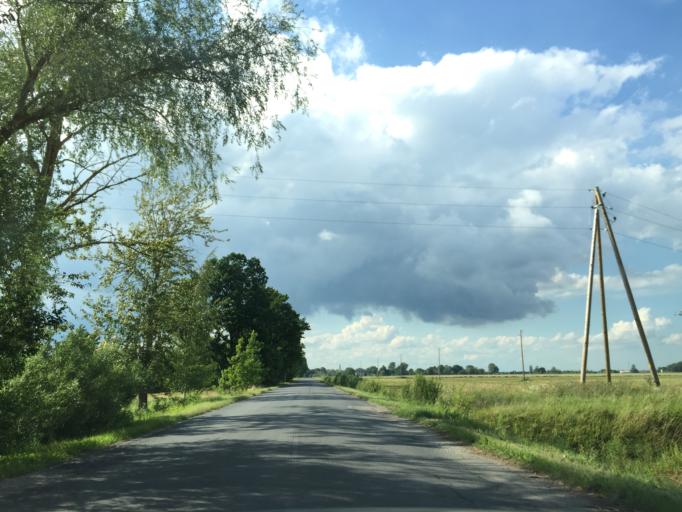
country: LV
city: Tervete
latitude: 56.5596
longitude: 23.3907
